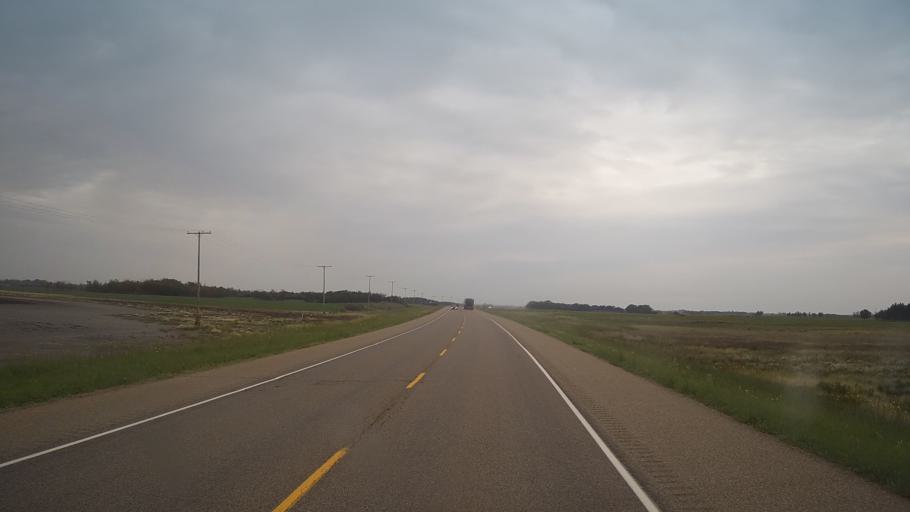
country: CA
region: Saskatchewan
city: Langham
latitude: 52.1293
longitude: -107.1055
